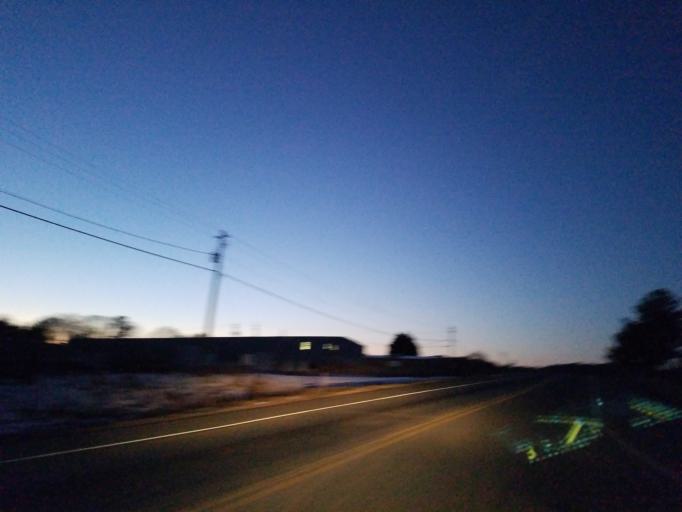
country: US
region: Georgia
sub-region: Cherokee County
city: Ball Ground
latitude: 34.2950
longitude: -84.4178
